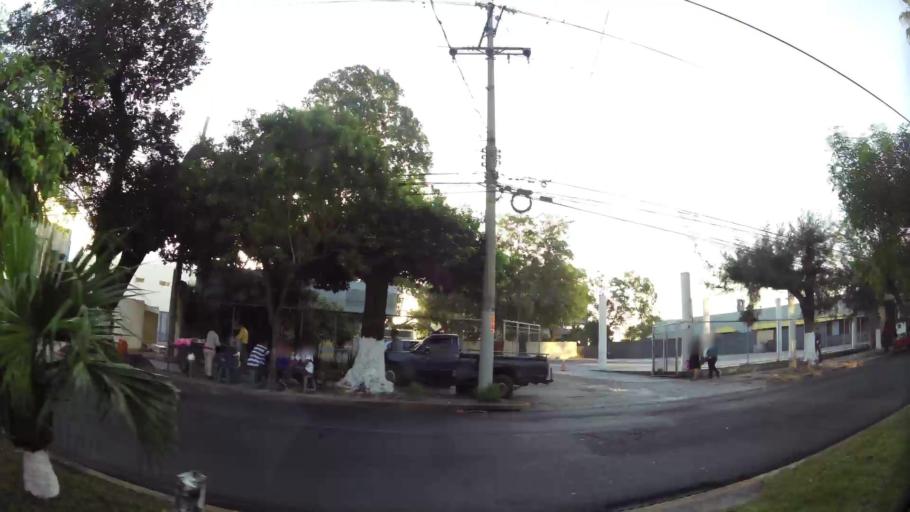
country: SV
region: San Salvador
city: San Salvador
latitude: 13.6987
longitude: -89.2265
